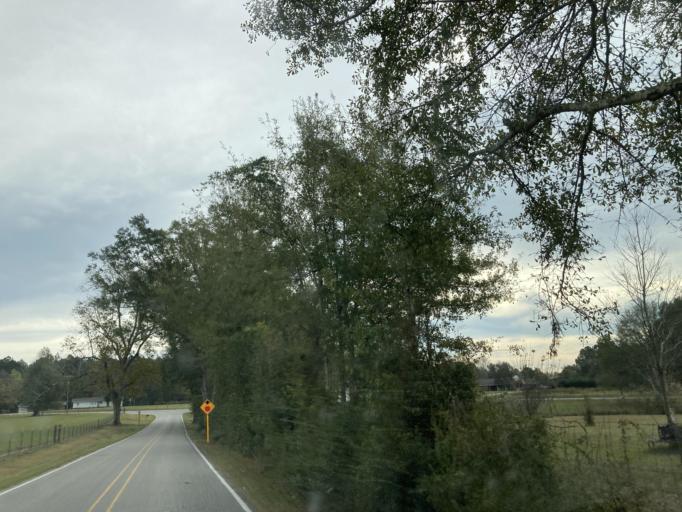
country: US
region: Mississippi
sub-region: Lamar County
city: Purvis
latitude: 31.1112
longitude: -89.4747
